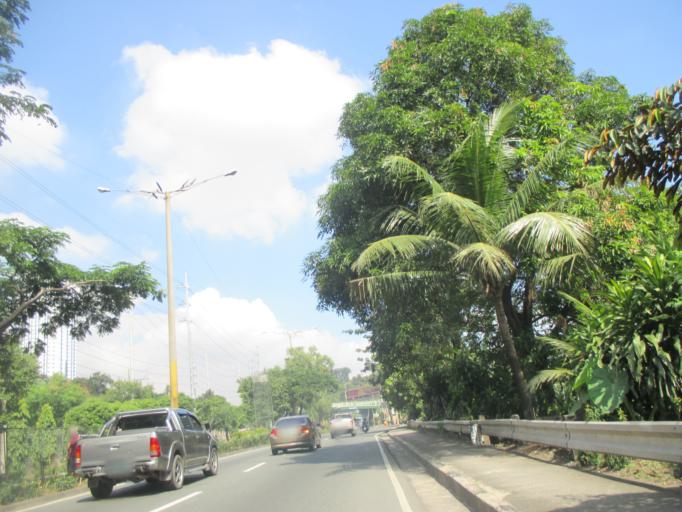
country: PH
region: Metro Manila
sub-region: Marikina
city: Calumpang
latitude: 14.6301
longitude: 121.0794
